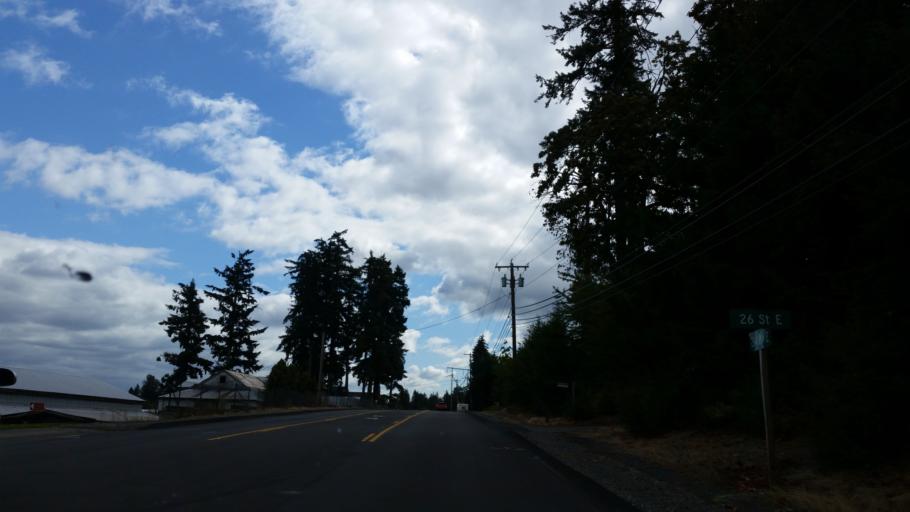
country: US
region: Washington
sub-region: Pierce County
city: Bonney Lake
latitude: 47.2347
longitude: -122.1444
